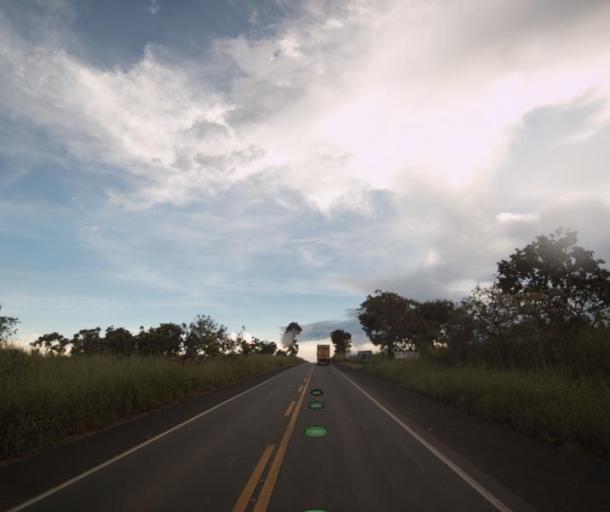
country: BR
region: Goias
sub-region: Uruacu
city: Uruacu
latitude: -14.1525
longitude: -49.1197
